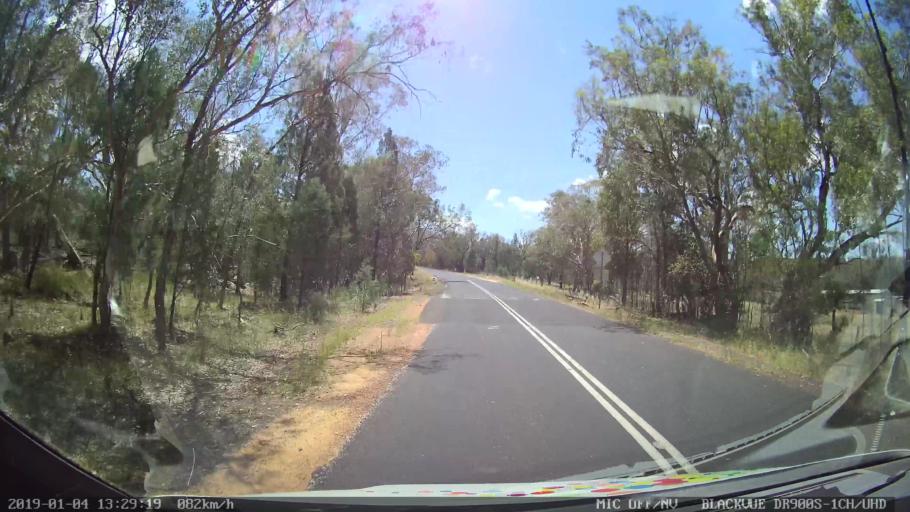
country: AU
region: New South Wales
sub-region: Parkes
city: Peak Hill
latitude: -32.6481
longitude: 148.5511
